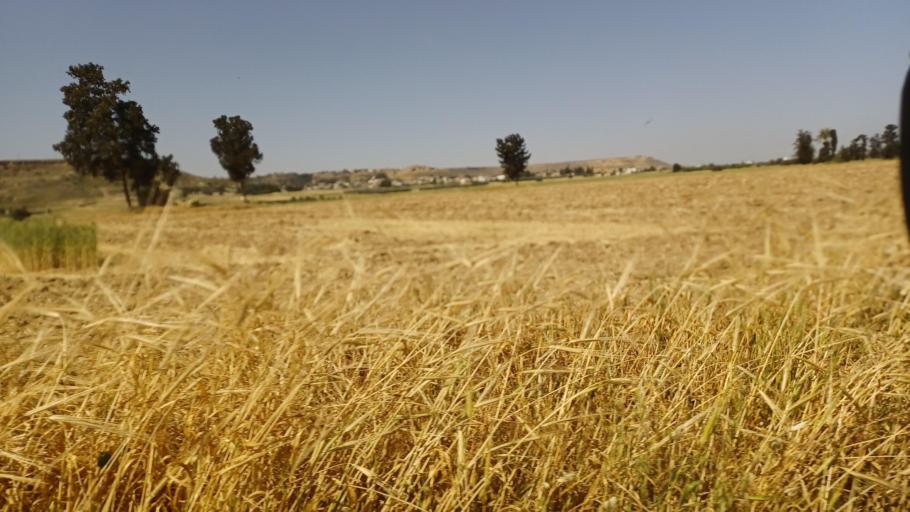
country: CY
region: Lefkosia
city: Mammari
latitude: 35.1822
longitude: 33.2201
